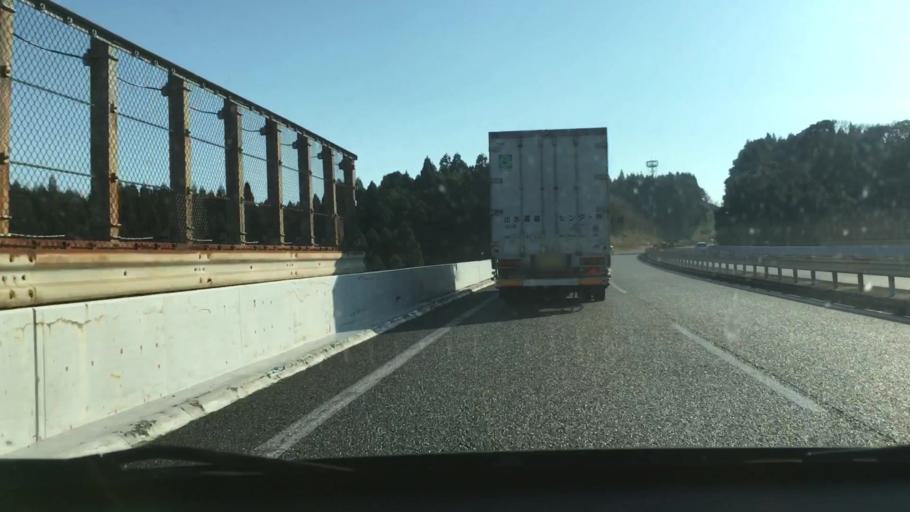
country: JP
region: Kagoshima
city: Kajiki
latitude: 31.9023
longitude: 130.7076
